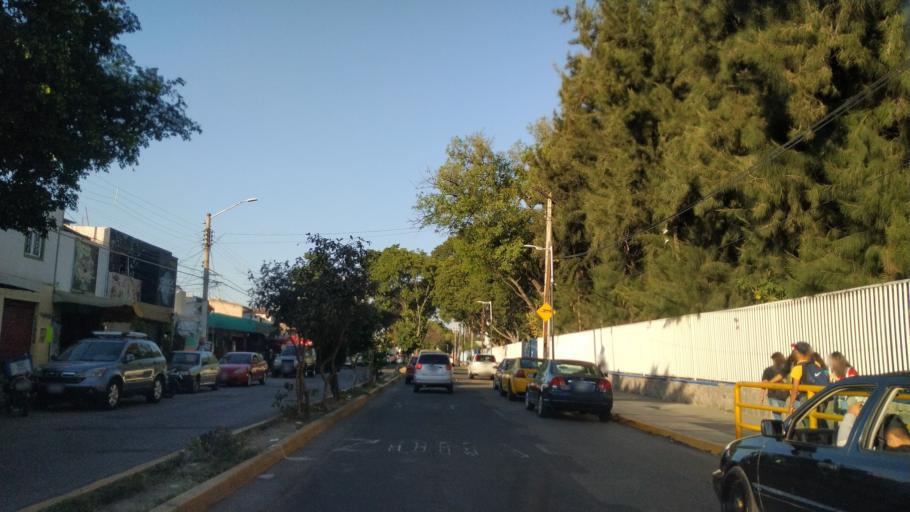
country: MX
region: Jalisco
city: Tlaquepaque
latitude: 20.6581
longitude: -103.3284
